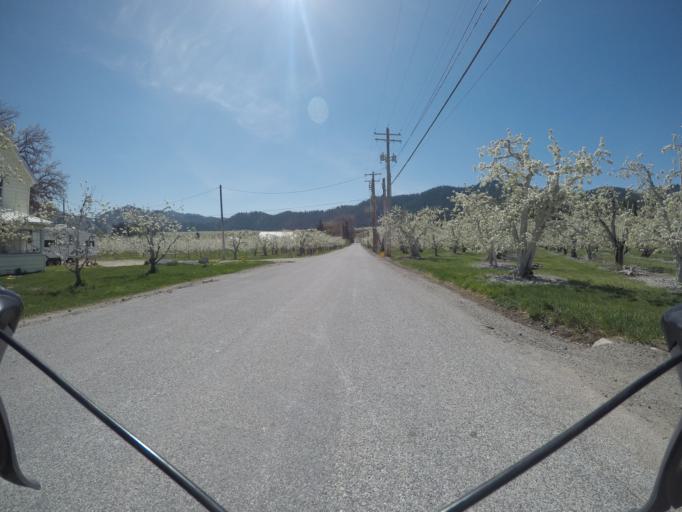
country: US
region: Washington
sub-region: Chelan County
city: Cashmere
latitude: 47.5379
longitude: -120.5611
